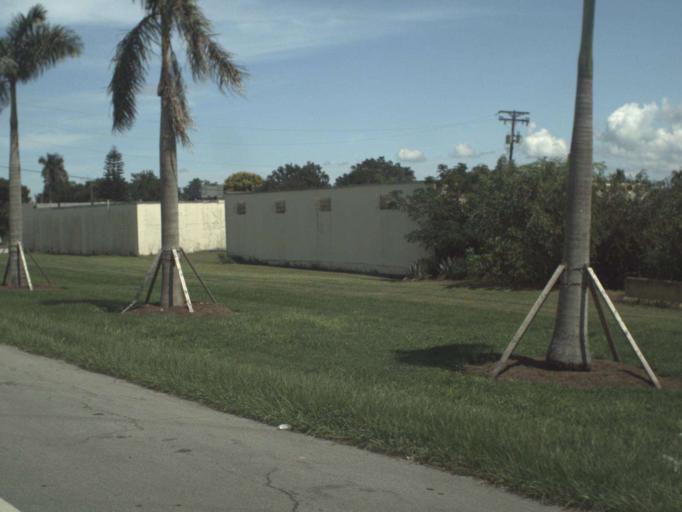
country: US
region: Florida
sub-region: Palm Beach County
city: Pahokee
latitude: 26.8174
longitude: -80.6656
